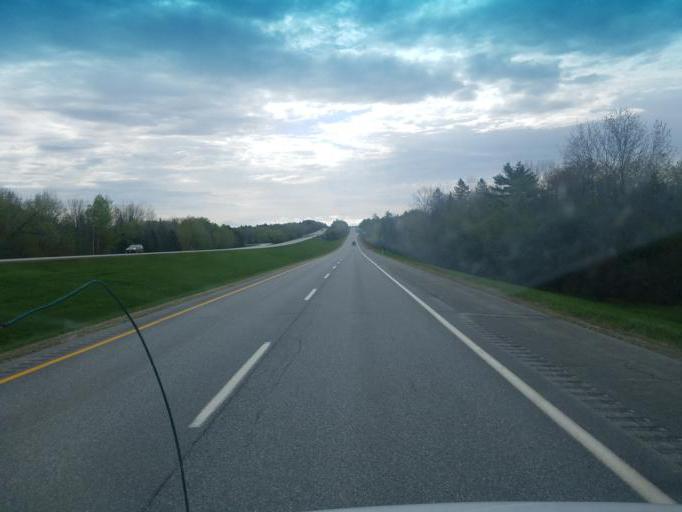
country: US
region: Maine
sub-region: Penobscot County
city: Etna
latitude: 44.7859
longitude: -69.1139
